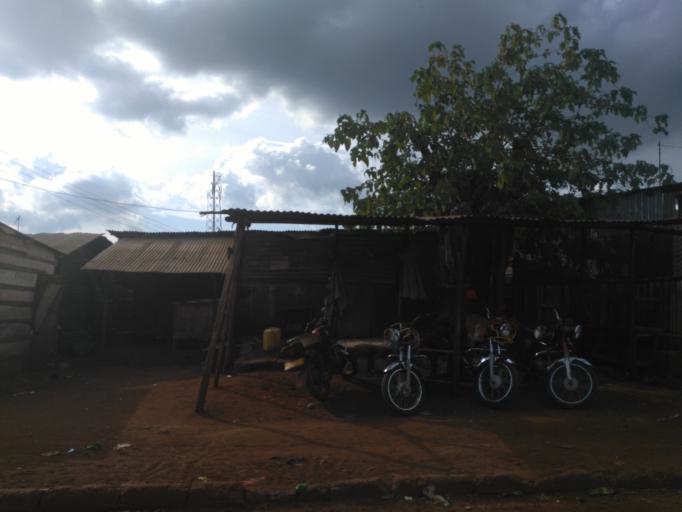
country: UG
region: Eastern Region
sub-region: Jinja District
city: Jinja
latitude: 0.4188
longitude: 33.2136
